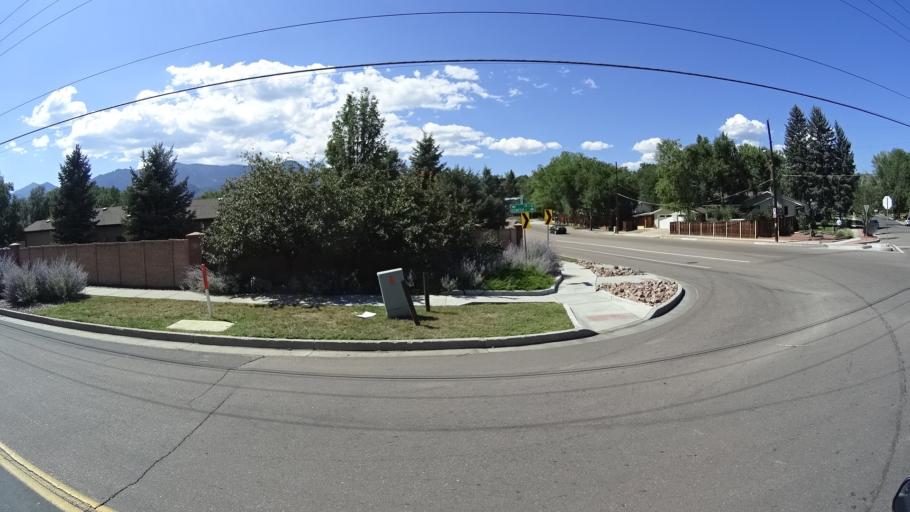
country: US
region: Colorado
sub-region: El Paso County
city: Colorado Springs
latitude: 38.8566
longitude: -104.8497
